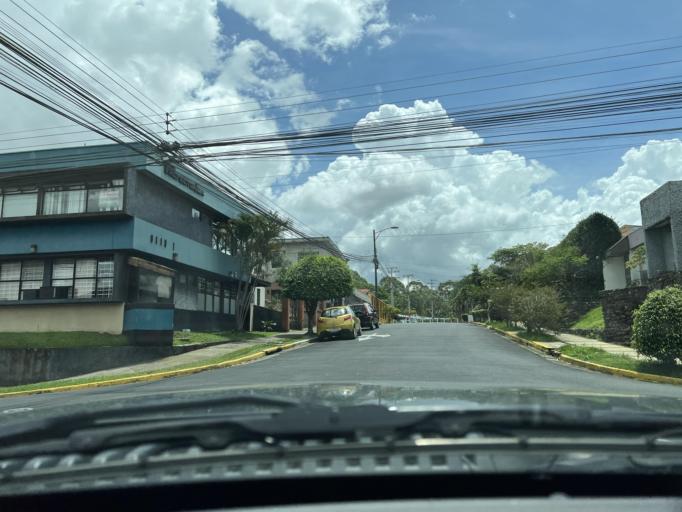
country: CR
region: San Jose
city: San Pedro
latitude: 9.9246
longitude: -84.0656
